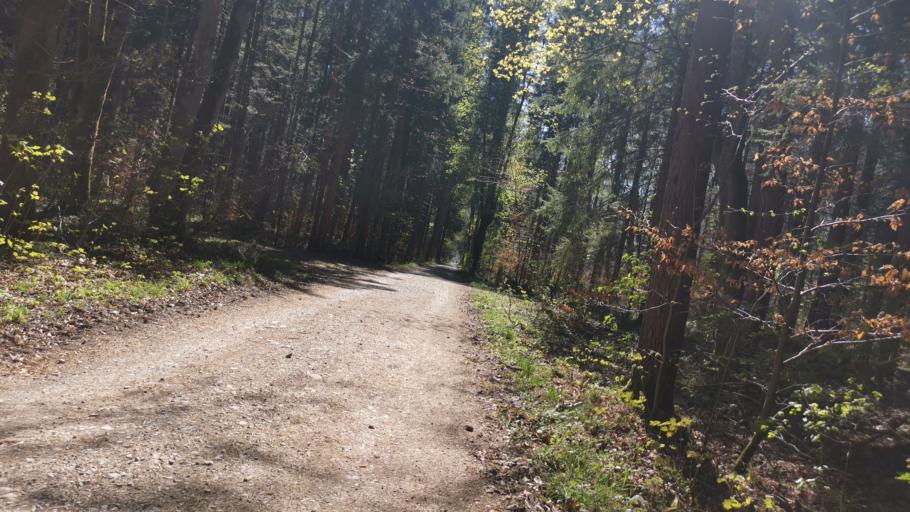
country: DE
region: Bavaria
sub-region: Upper Bavaria
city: Planegg
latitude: 48.0843
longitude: 11.4276
